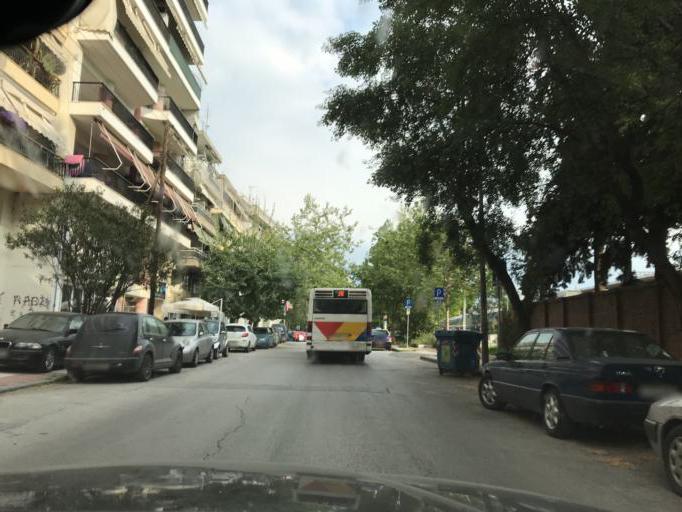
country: GR
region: Central Macedonia
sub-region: Nomos Thessalonikis
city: Thessaloniki
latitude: 40.6458
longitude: 22.9291
